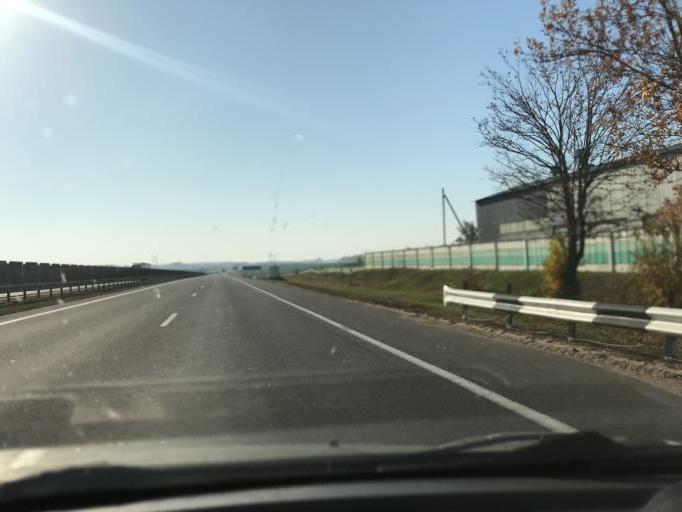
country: BY
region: Minsk
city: Pryvol'ny
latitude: 53.8139
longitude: 27.8134
